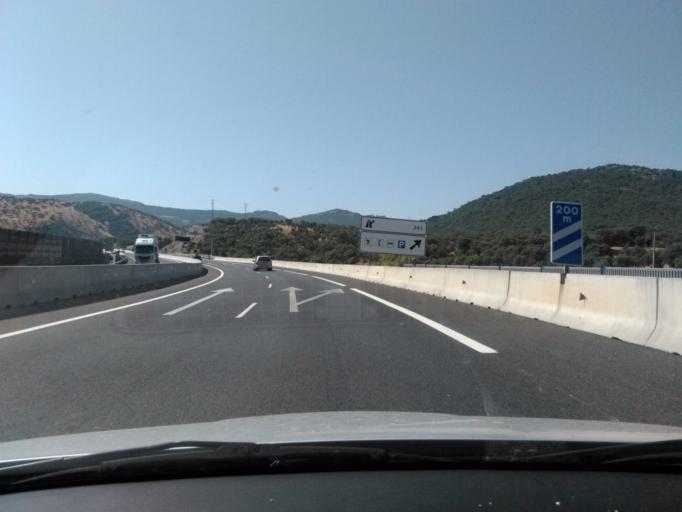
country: ES
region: Andalusia
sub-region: Provincia de Jaen
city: Santa Elena
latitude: 38.4191
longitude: -3.5008
